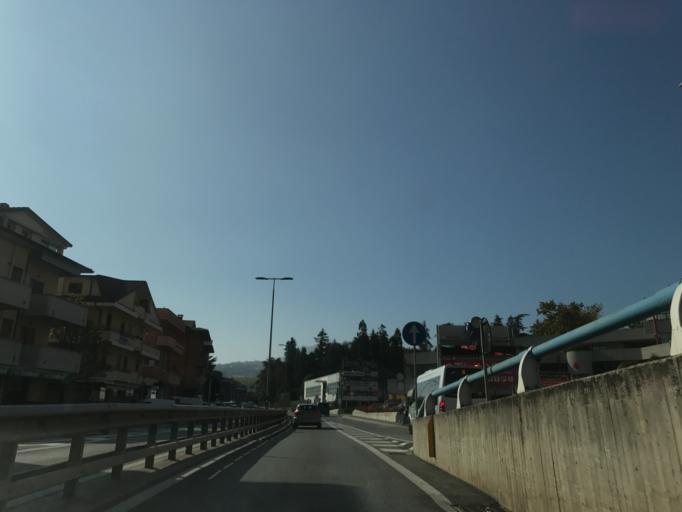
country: SM
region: Serravalle
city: Serravalle
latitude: 43.9771
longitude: 12.4871
